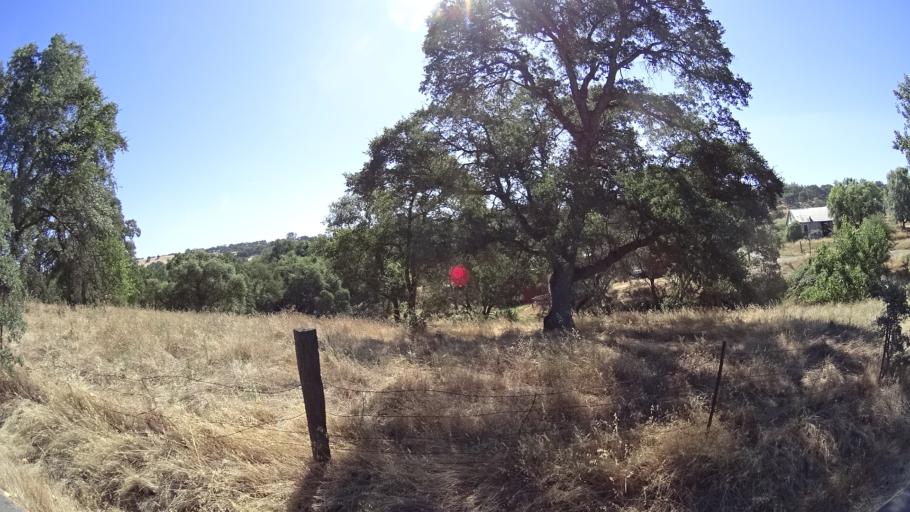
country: US
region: California
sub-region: Amador County
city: Jackson
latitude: 38.2604
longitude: -120.7635
